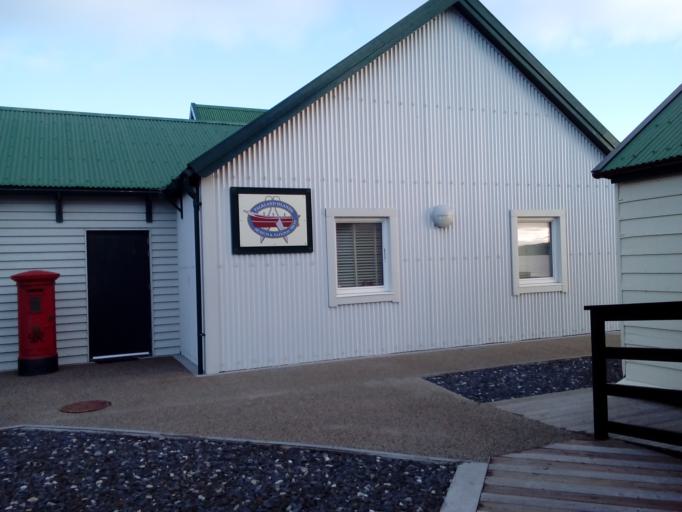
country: FK
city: Stanley
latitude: -51.6909
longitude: -57.8652
